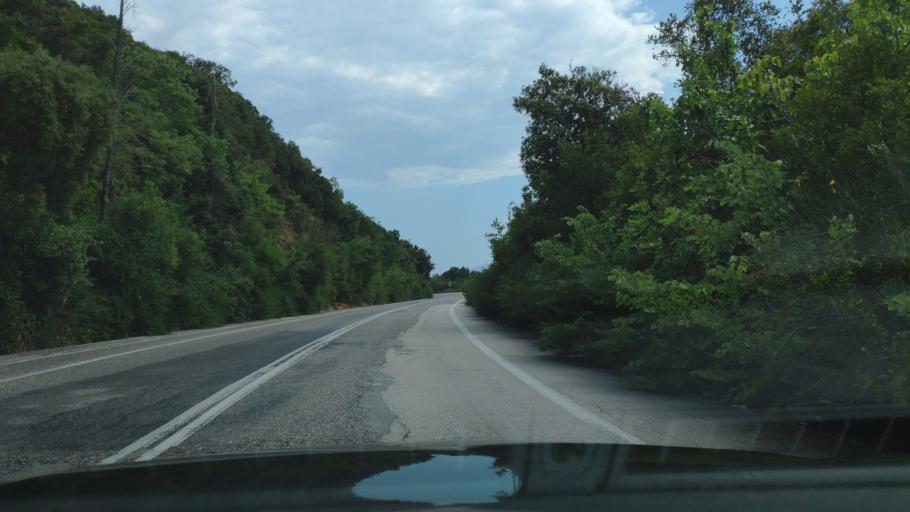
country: GR
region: West Greece
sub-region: Nomos Aitolias kai Akarnanias
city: Menidi
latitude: 39.0046
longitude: 21.1476
